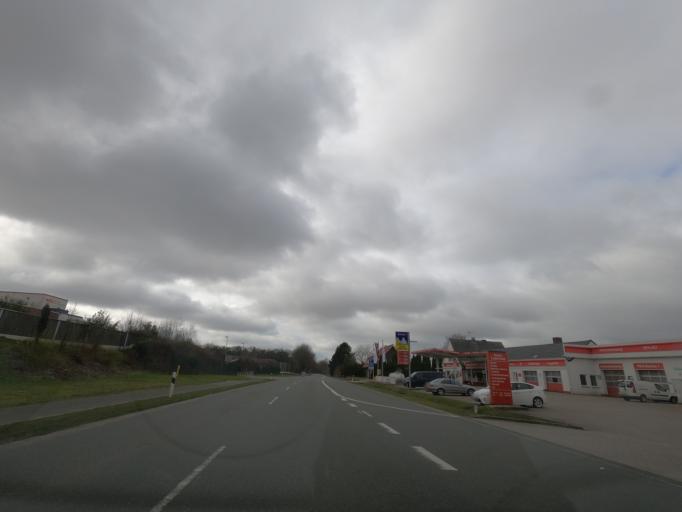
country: DE
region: Lower Saxony
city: Loningen
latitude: 52.7325
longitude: 7.7429
